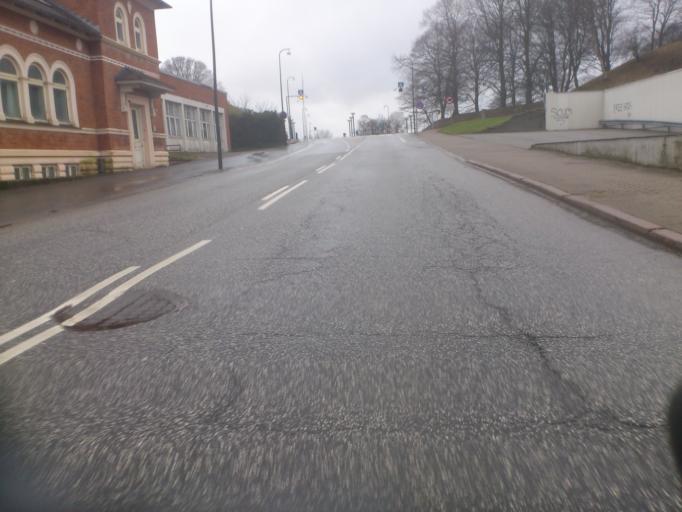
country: DK
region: South Denmark
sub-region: Fredericia Kommune
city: Fredericia
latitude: 55.5642
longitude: 9.7497
